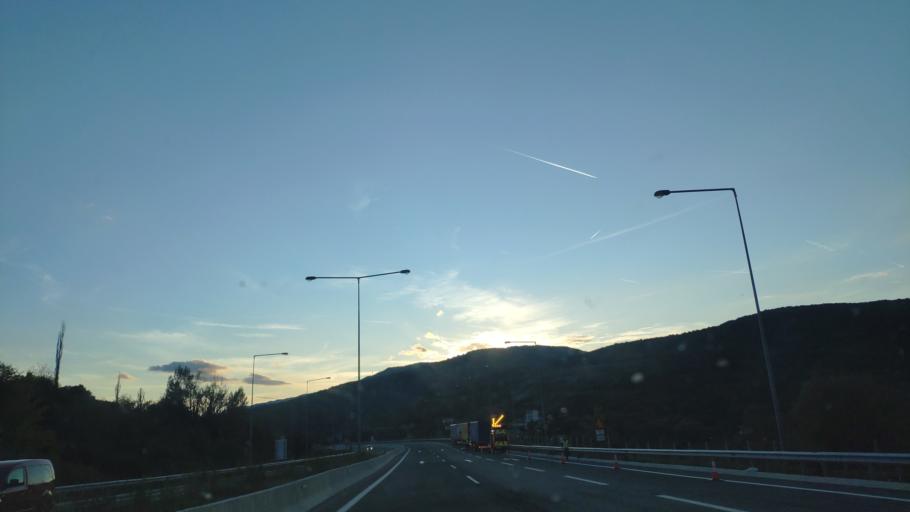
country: GR
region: Epirus
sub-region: Nomos Ioanninon
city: Metsovo
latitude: 39.7533
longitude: 21.0851
